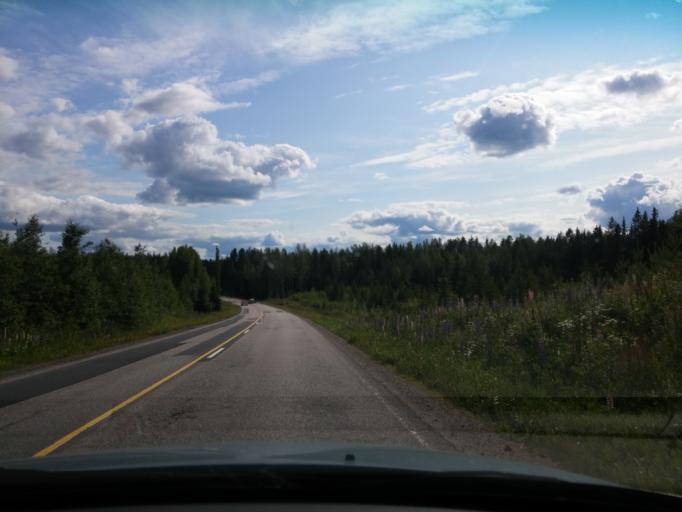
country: FI
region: Central Finland
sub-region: Keuruu
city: Keuruu
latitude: 62.3343
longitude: 24.7335
